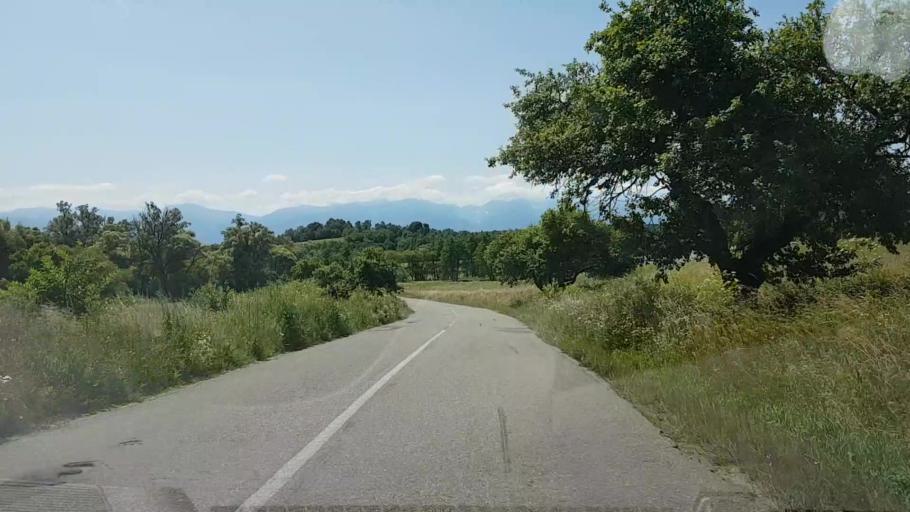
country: RO
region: Brasov
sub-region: Comuna Voila
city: Voila
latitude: 45.8633
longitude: 24.8254
